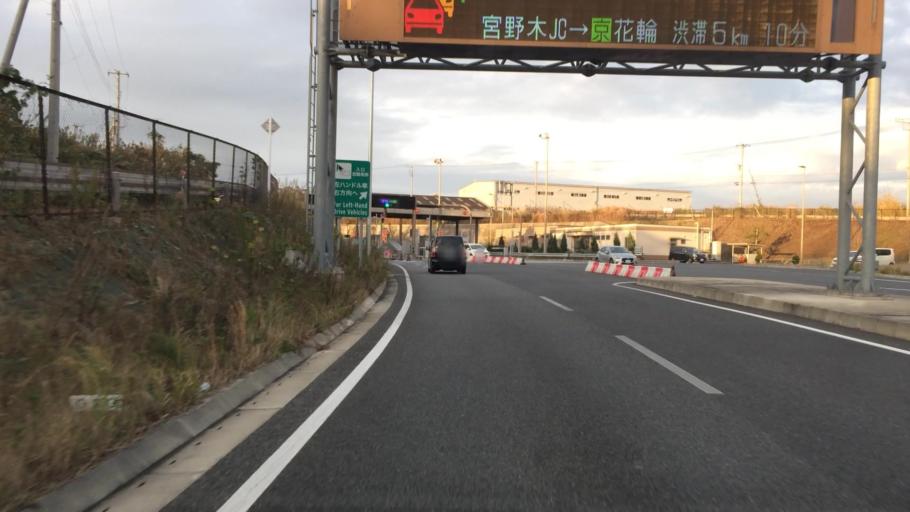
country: JP
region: Chiba
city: Shisui
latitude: 35.7238
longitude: 140.2946
